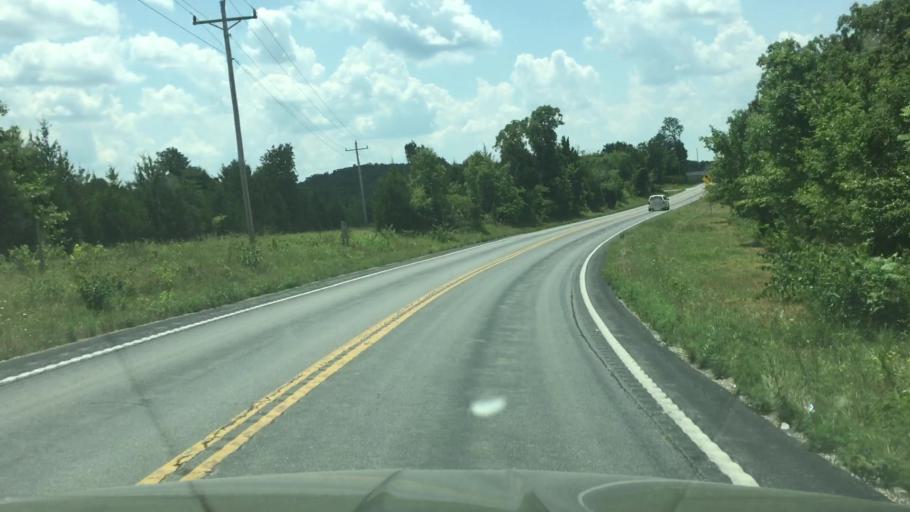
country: US
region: Missouri
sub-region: Miller County
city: Tuscumbia
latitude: 38.1043
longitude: -92.4987
